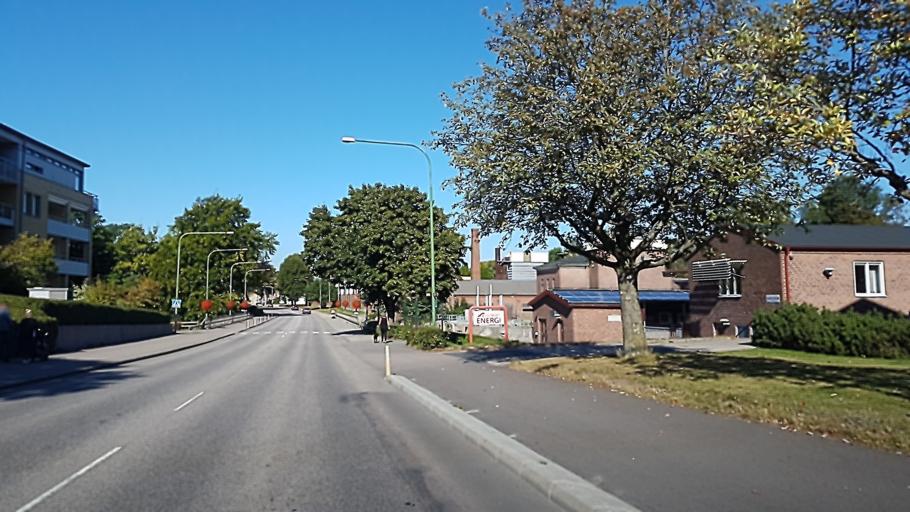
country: SE
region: Kronoberg
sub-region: Ljungby Kommun
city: Ljungby
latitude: 56.8300
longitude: 13.9509
